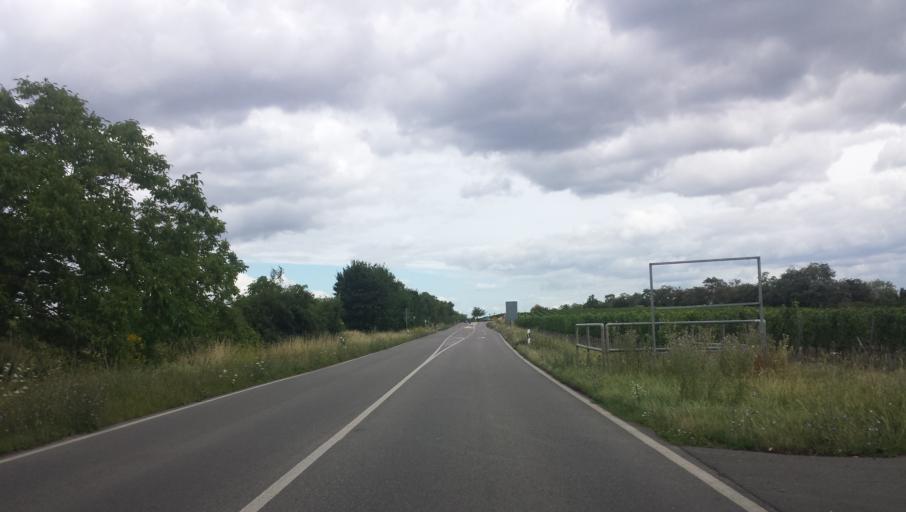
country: DE
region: Rheinland-Pfalz
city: Deidesheim
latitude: 49.3959
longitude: 8.1837
